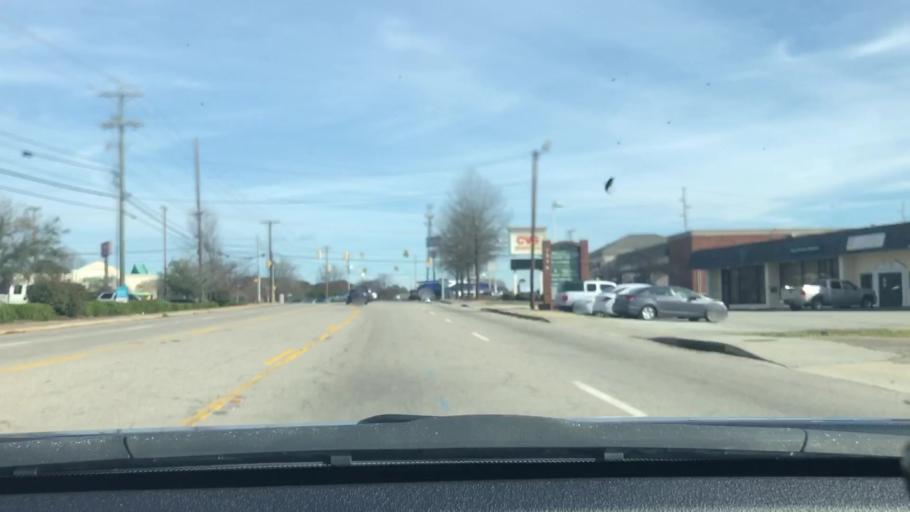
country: US
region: South Carolina
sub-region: Lexington County
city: Saint Andrews
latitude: 34.0497
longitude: -81.1071
